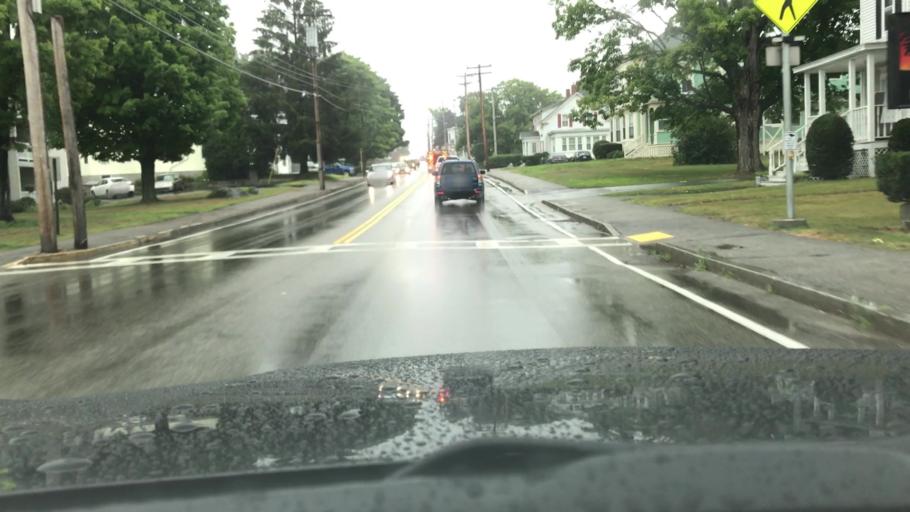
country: US
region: Maine
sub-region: York County
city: Biddeford
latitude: 43.4886
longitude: -70.4657
